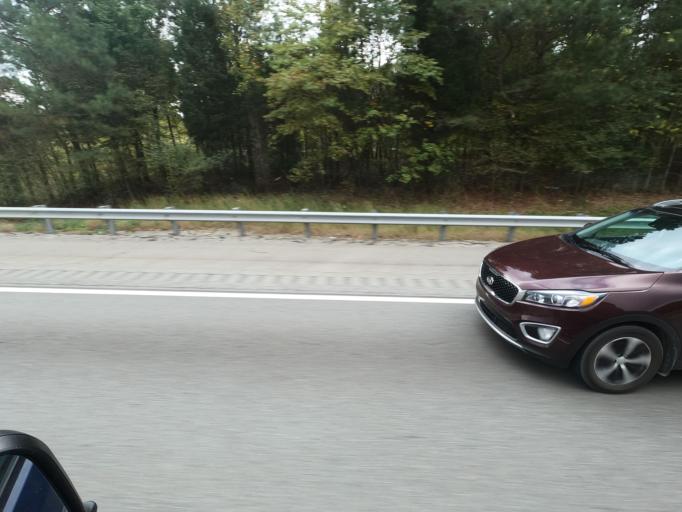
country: US
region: Tennessee
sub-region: Dickson County
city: Dickson
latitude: 35.9962
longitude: -87.4688
